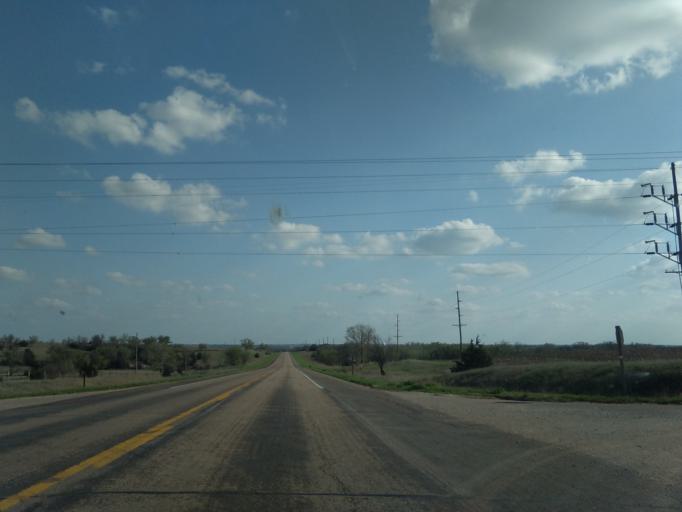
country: US
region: Nebraska
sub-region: Webster County
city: Red Cloud
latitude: 40.1181
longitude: -98.5189
